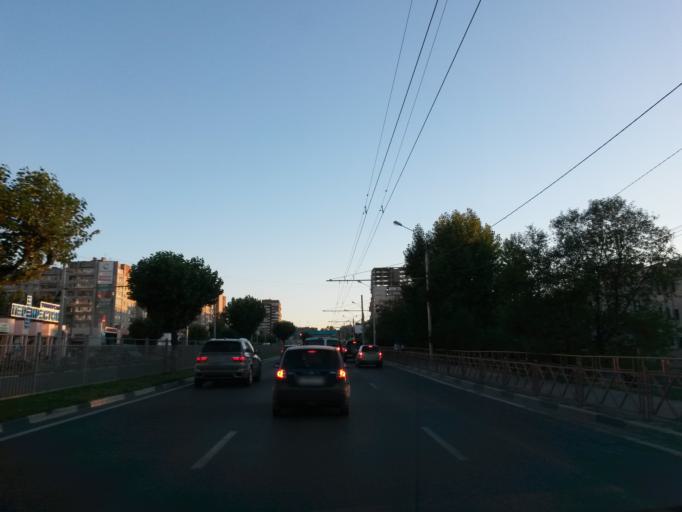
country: RU
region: Jaroslavl
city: Yaroslavl
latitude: 57.5964
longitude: 39.8690
